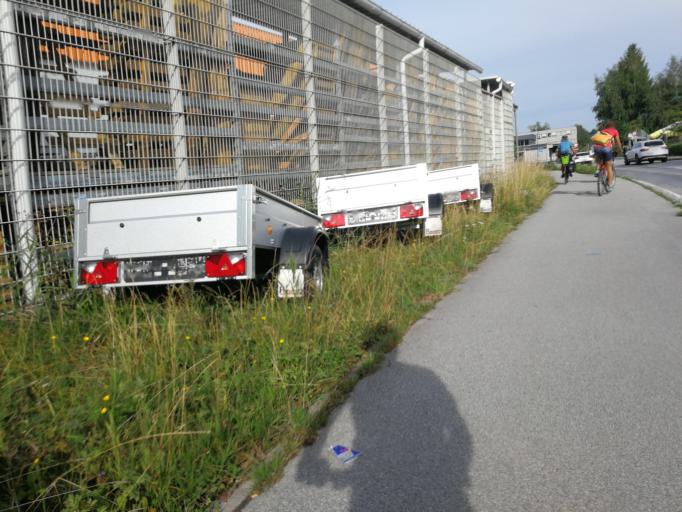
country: AT
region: Salzburg
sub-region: Politischer Bezirk Salzburg-Umgebung
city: Bergheim
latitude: 47.8396
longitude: 13.0589
